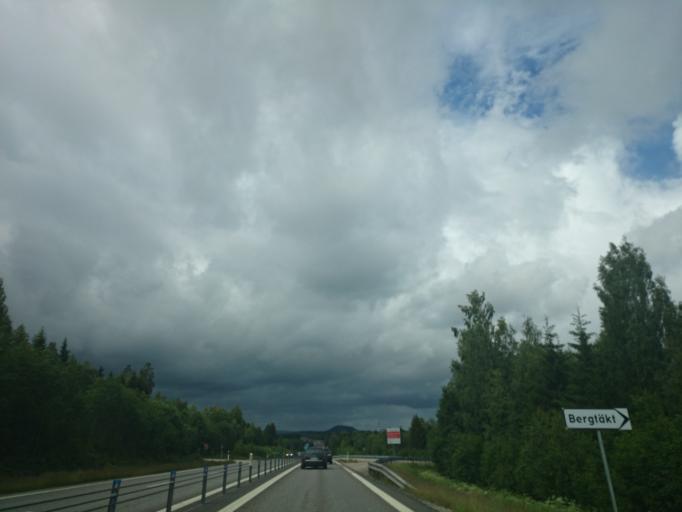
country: SE
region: Vaesternorrland
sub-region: Sundsvalls Kommun
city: Njurundabommen
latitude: 62.2387
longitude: 17.3747
